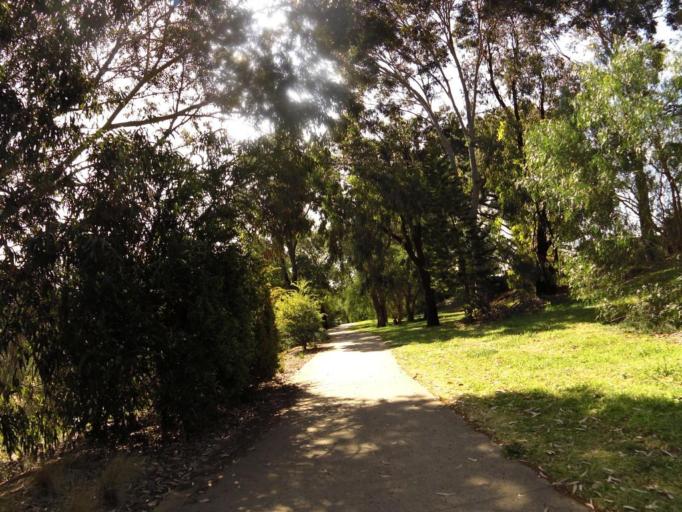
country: AU
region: Victoria
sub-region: Wyndham
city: Werribee
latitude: -37.9139
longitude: 144.6544
